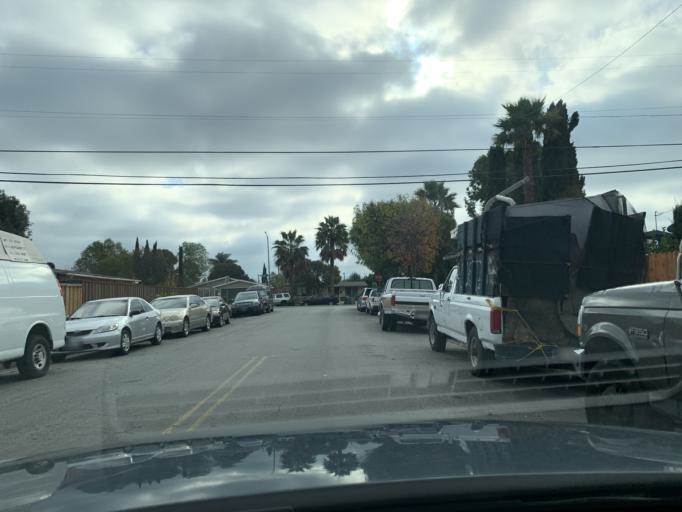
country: US
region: California
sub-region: Santa Clara County
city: Alum Rock
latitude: 37.3368
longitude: -121.8344
